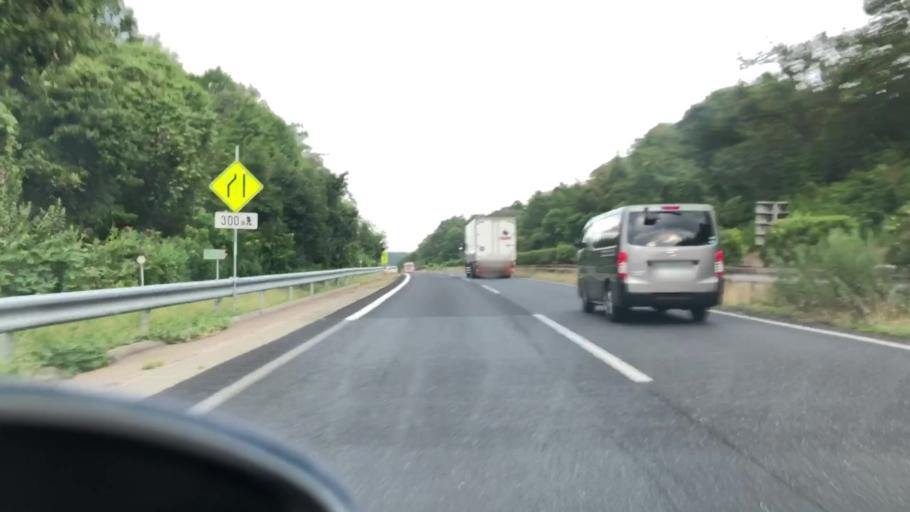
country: JP
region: Hyogo
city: Yashiro
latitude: 34.9148
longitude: 135.0281
